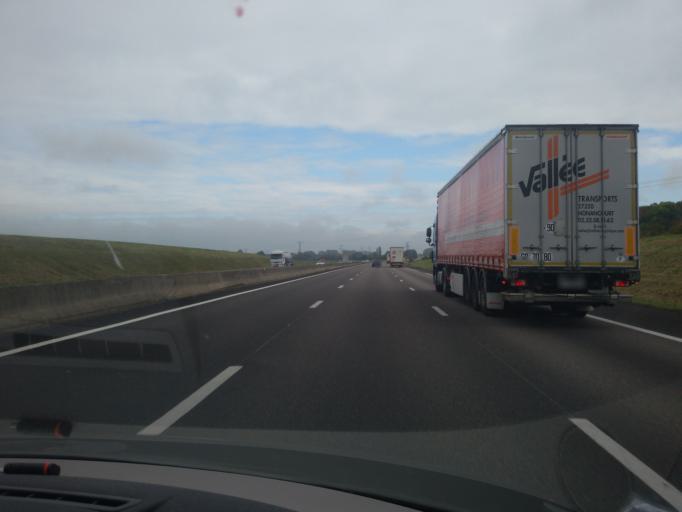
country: FR
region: Haute-Normandie
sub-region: Departement de l'Eure
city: Hauville
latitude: 49.3704
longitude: 0.7213
